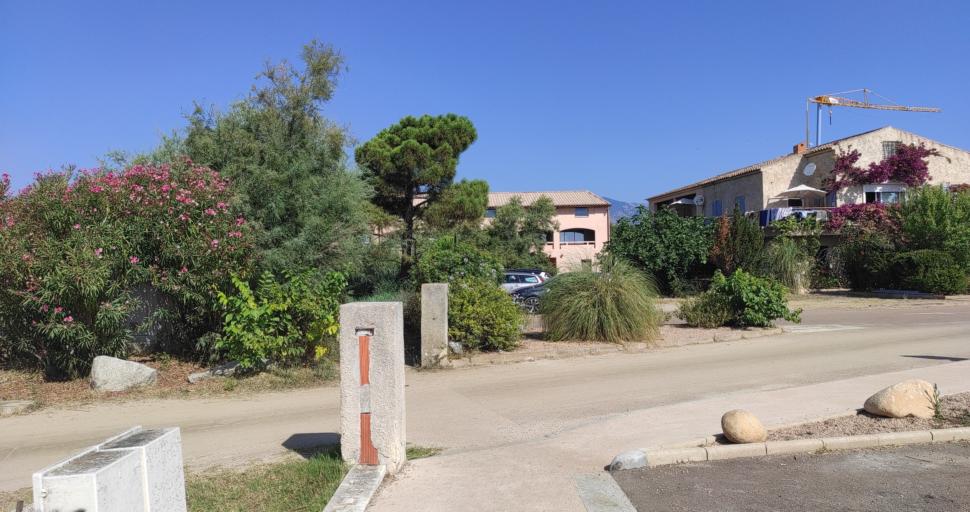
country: FR
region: Corsica
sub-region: Departement de la Corse-du-Sud
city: Porto-Vecchio
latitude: 41.6375
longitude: 9.3474
